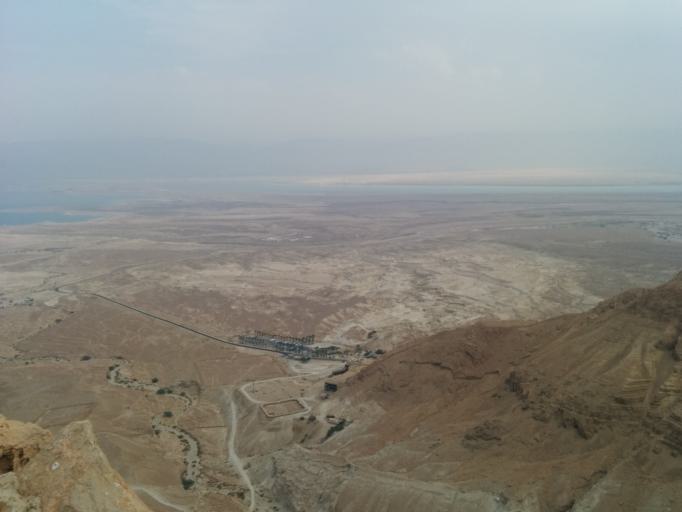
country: IL
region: Southern District
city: `En Boqeq
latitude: 31.3136
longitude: 35.3541
